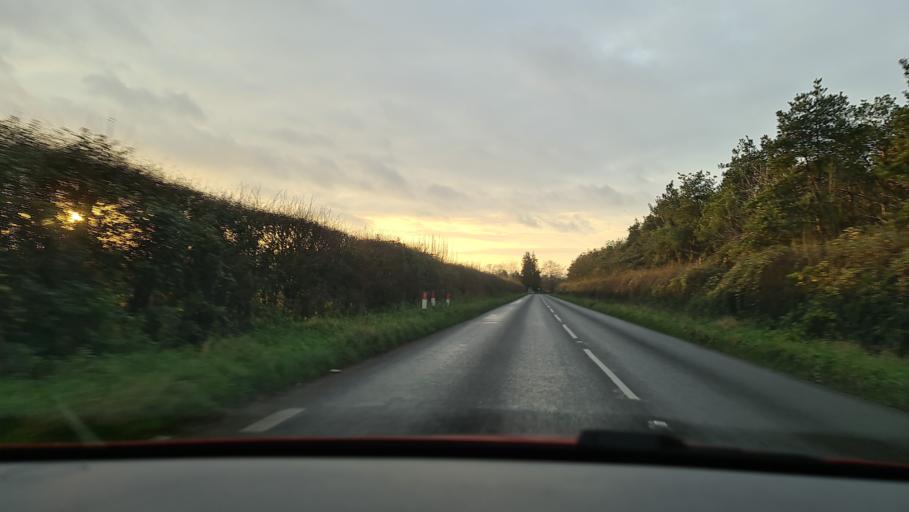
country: GB
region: England
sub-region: Oxfordshire
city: Kidlington
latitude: 51.8828
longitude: -1.2742
